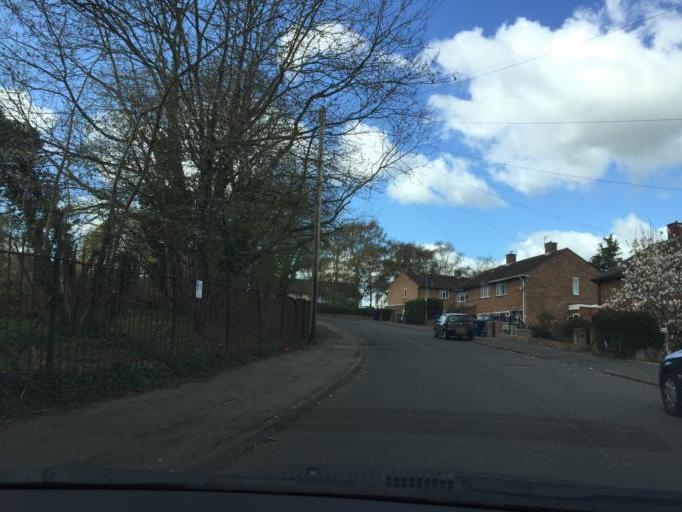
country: GB
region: England
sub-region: Oxfordshire
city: Cowley
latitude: 51.7688
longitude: -1.2177
